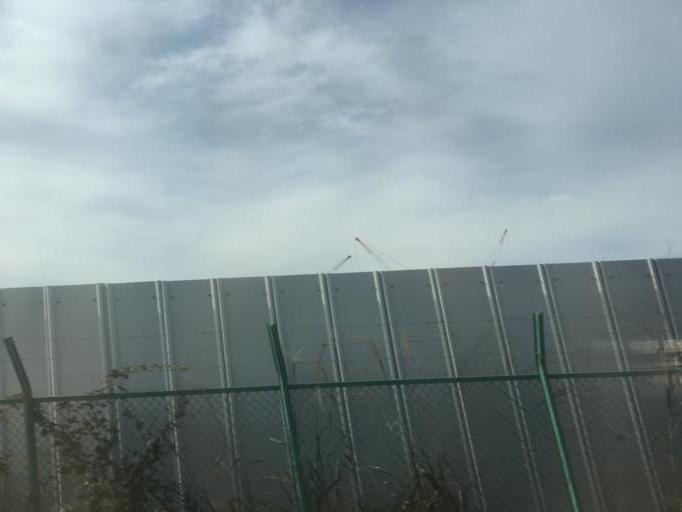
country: JP
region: Saitama
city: Sayama
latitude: 35.8386
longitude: 139.4060
